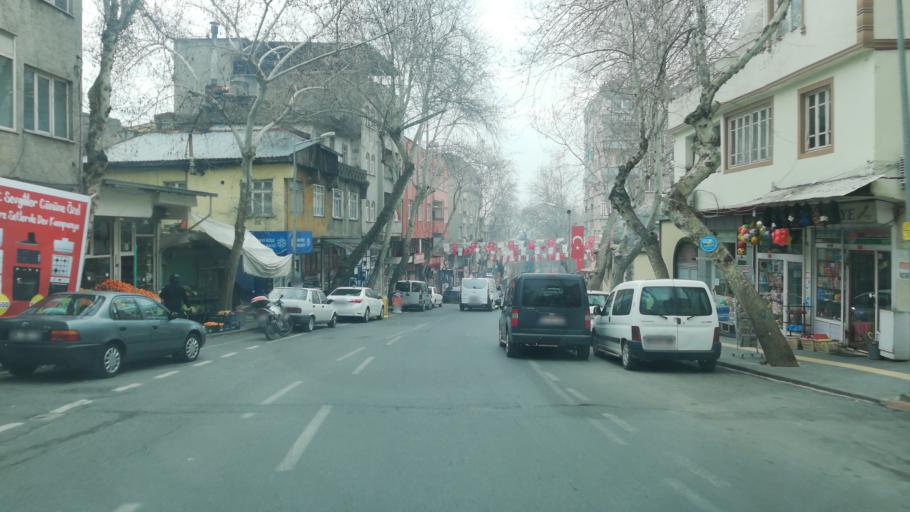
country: TR
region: Kahramanmaras
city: Kahramanmaras
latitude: 37.5893
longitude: 36.9270
